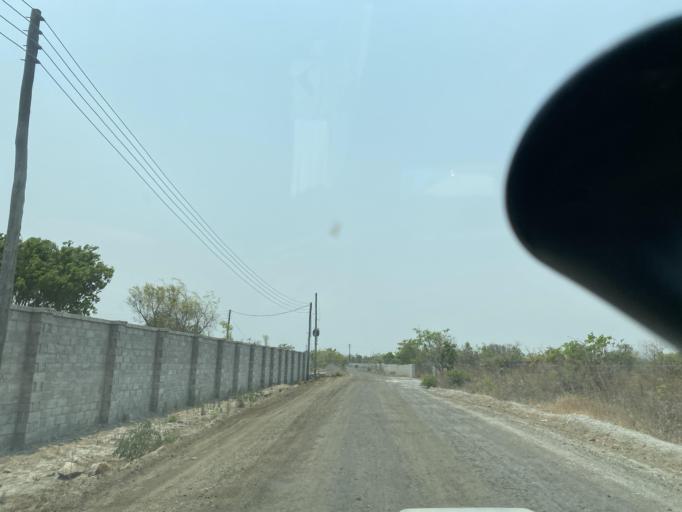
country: ZM
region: Lusaka
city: Lusaka
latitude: -15.5345
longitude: 28.4477
